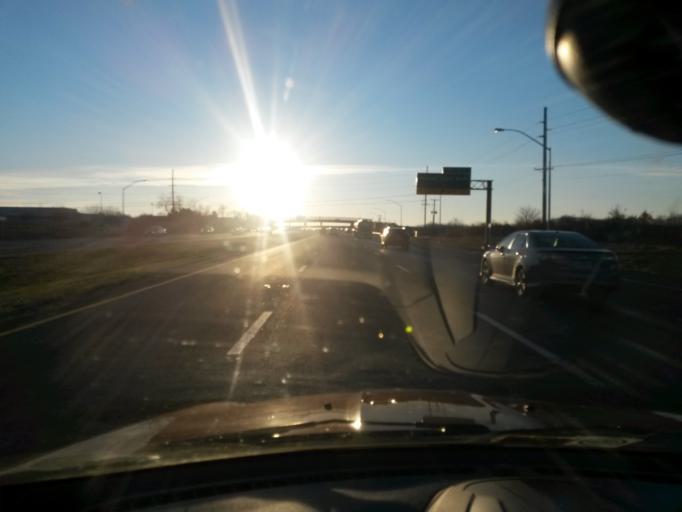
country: US
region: Virginia
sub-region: City of Roanoke
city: Roanoke
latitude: 37.3011
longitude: -79.9644
